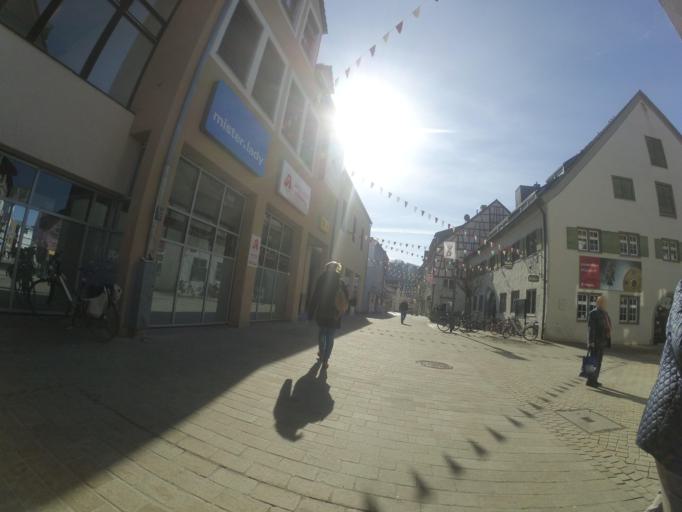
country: DE
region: Baden-Wuerttemberg
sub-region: Tuebingen Region
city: Weingarten
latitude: 47.8067
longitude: 9.6409
